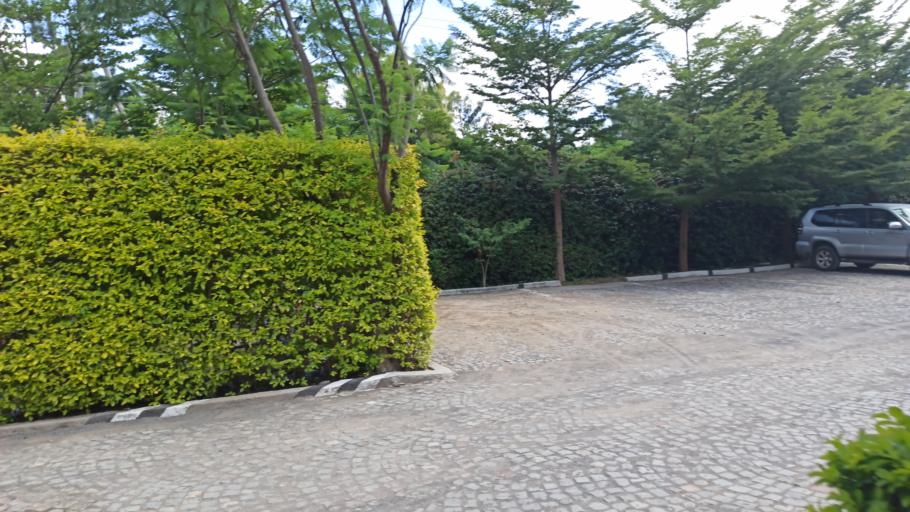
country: ET
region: Oromiya
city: Ziway
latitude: 7.9267
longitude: 38.7244
